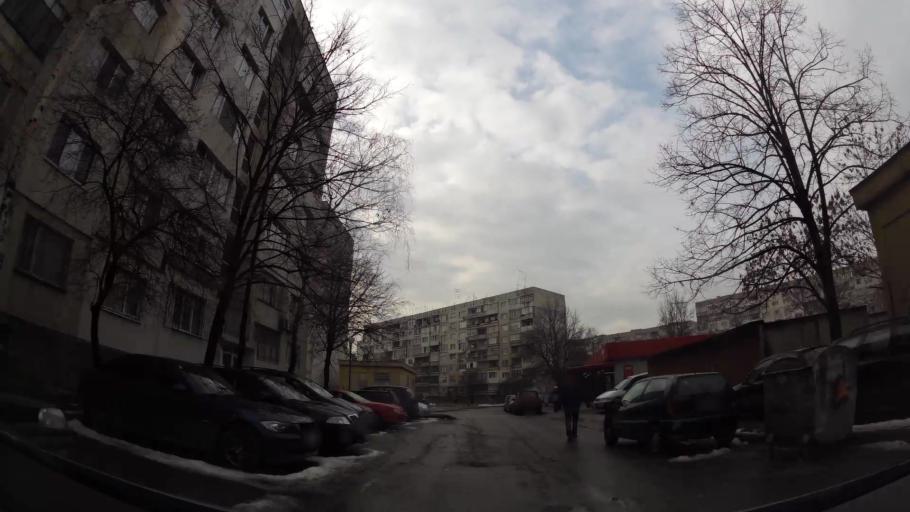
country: BG
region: Sofia-Capital
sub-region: Stolichna Obshtina
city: Sofia
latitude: 42.7133
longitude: 23.2613
